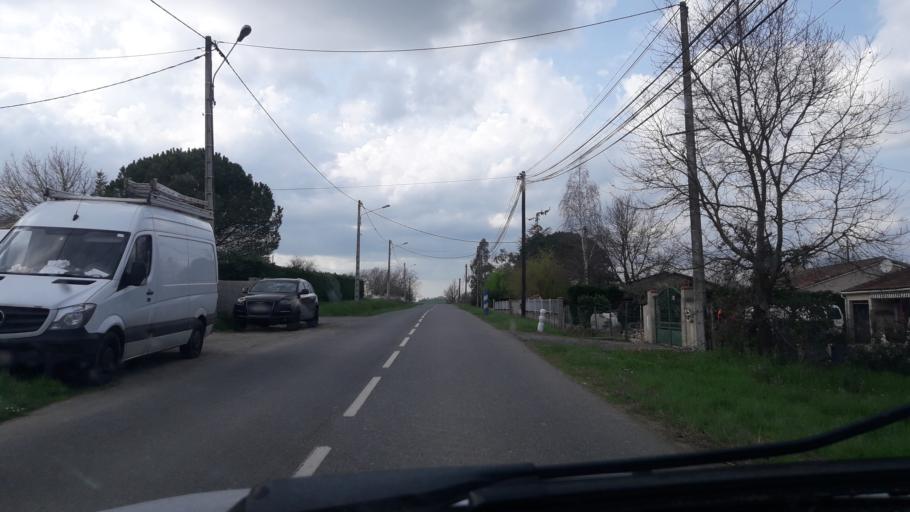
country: FR
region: Midi-Pyrenees
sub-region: Departement de la Haute-Garonne
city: Rieux-Volvestre
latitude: 43.2635
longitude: 1.2148
